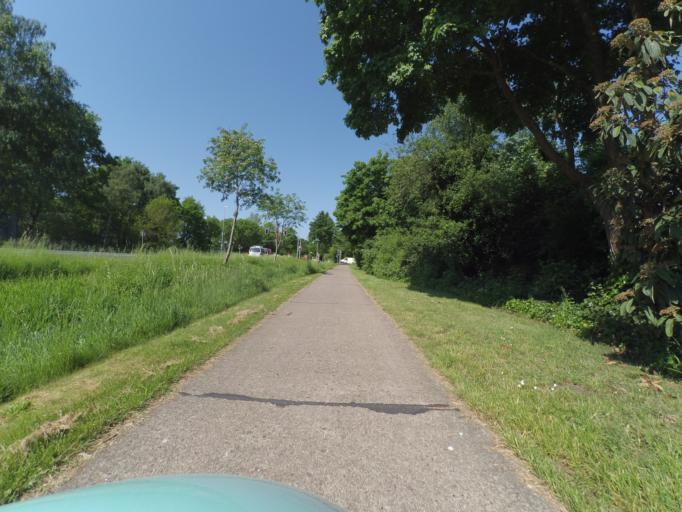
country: DE
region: Lower Saxony
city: Burgdorf
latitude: 52.4455
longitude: 9.9910
